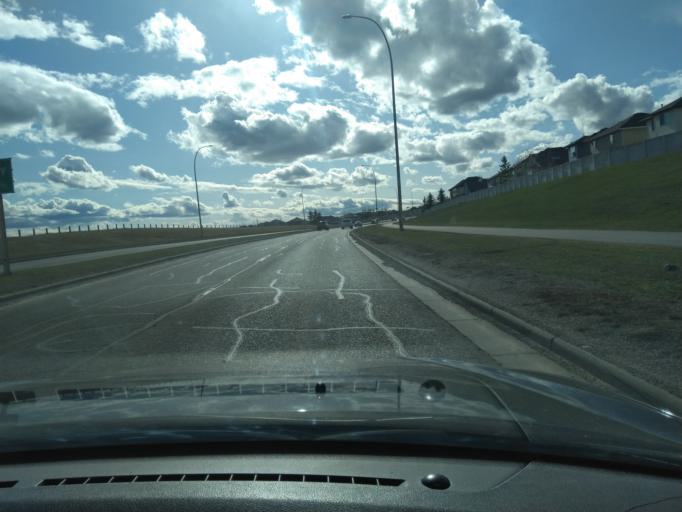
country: CA
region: Alberta
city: Calgary
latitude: 51.1432
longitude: -114.1914
